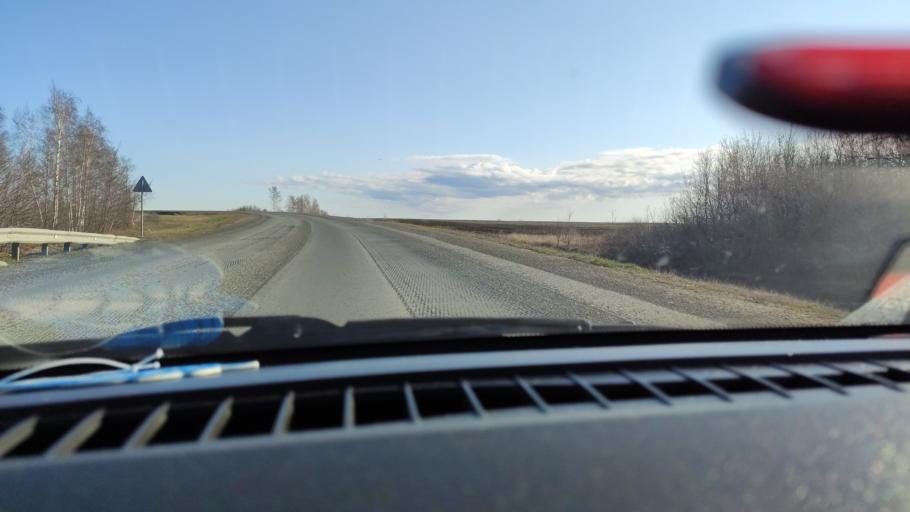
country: RU
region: Saratov
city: Dukhovnitskoye
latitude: 52.7109
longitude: 48.2656
